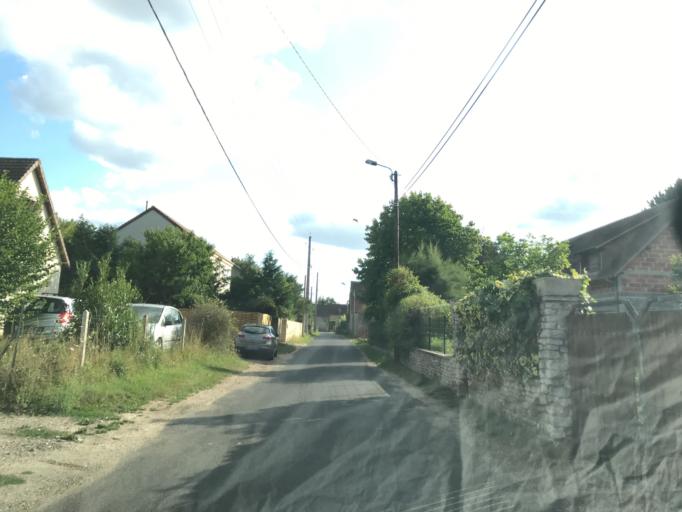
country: FR
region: Haute-Normandie
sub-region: Departement de l'Eure
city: Courcelles-sur-Seine
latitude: 49.1644
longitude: 1.4173
